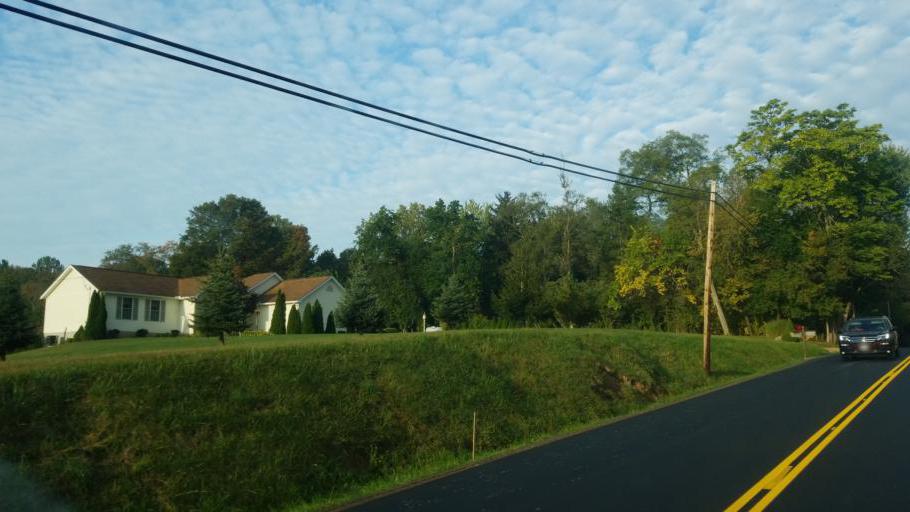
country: US
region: Ohio
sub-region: Knox County
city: Mount Vernon
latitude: 40.4029
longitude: -82.5678
